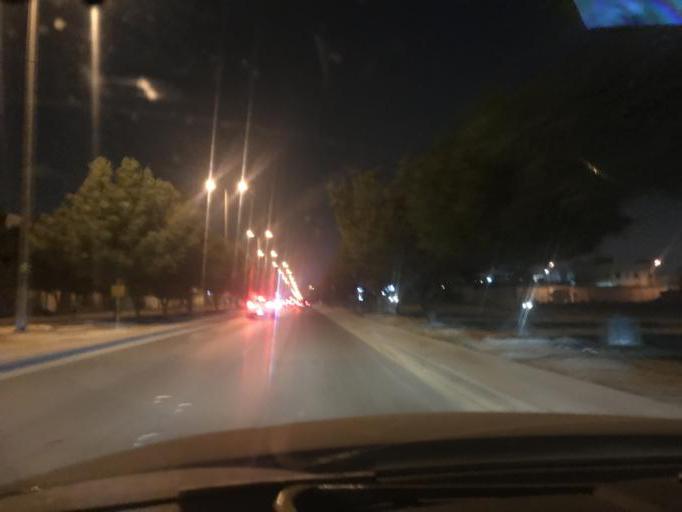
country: SA
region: Ar Riyad
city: Riyadh
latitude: 24.6805
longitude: 46.7930
